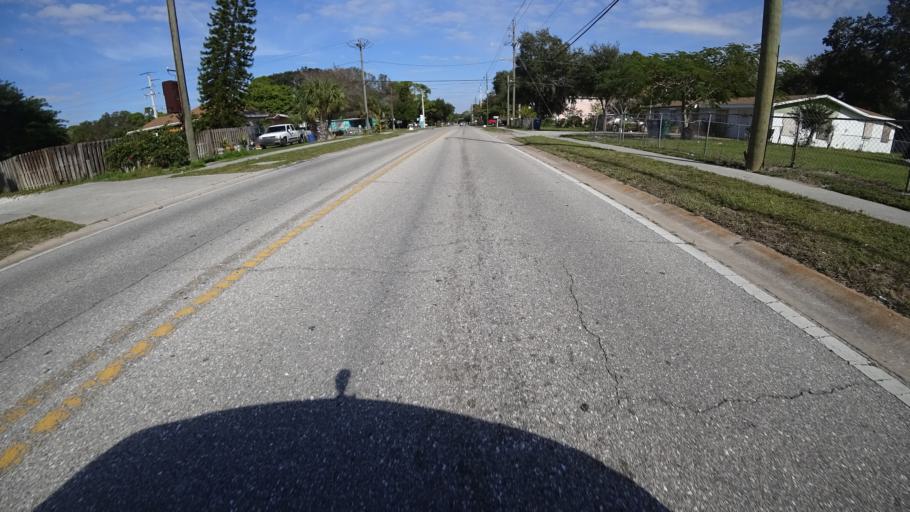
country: US
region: Florida
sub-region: Manatee County
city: Whitfield
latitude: 27.4360
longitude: -82.5590
